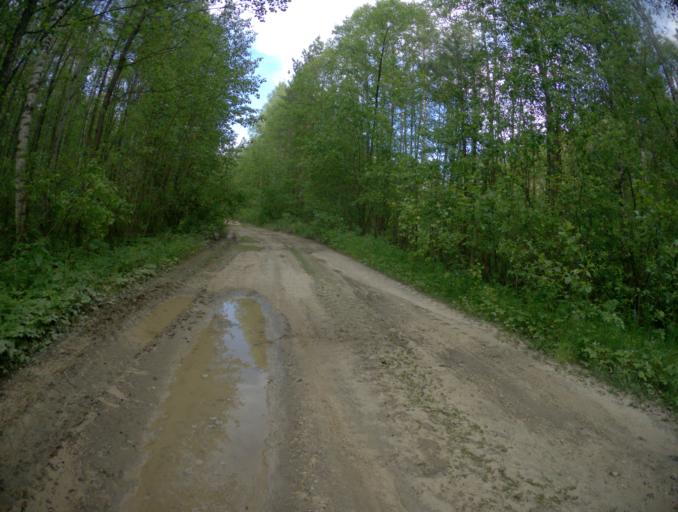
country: RU
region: Vladimir
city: Zolotkovo
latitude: 55.4917
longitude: 40.9592
